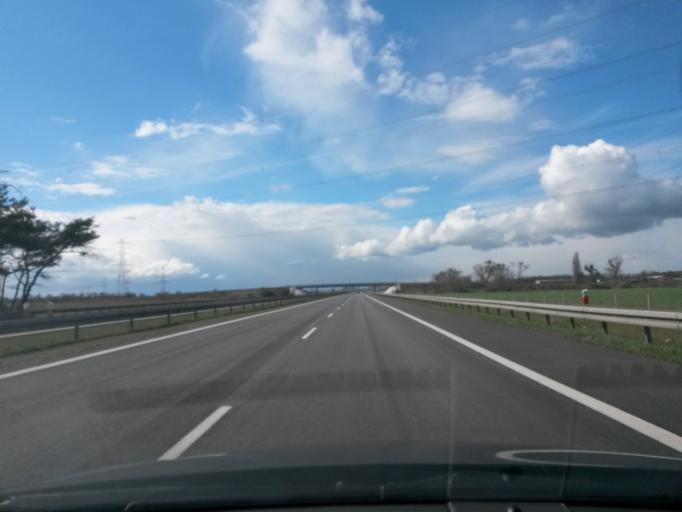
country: PL
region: Greater Poland Voivodeship
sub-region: Powiat wrzesinski
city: Kolaczkowo
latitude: 52.2805
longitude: 17.6935
